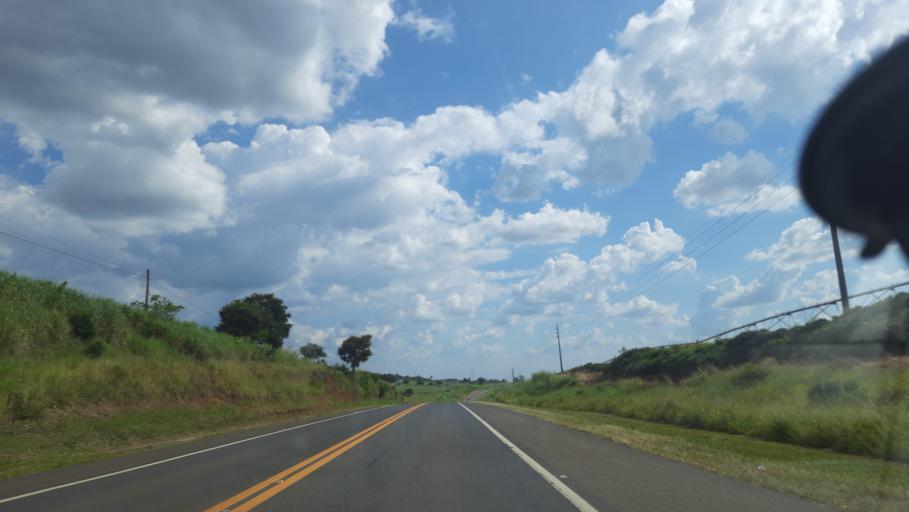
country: BR
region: Sao Paulo
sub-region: Sao Jose Do Rio Pardo
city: Sao Jose do Rio Pardo
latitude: -21.6755
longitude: -46.9246
